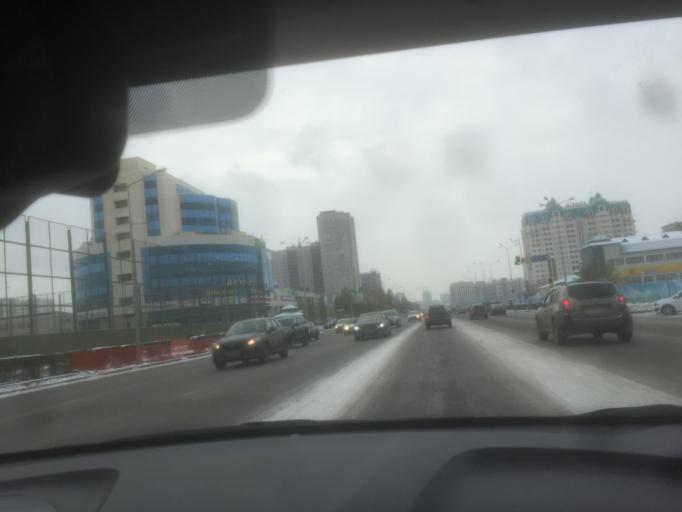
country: KZ
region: Astana Qalasy
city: Astana
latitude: 51.1425
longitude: 71.4625
